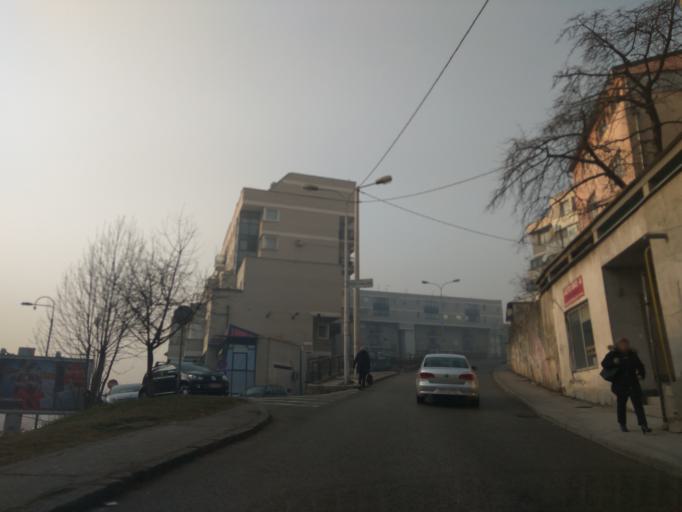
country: BA
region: Federation of Bosnia and Herzegovina
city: Kobilja Glava
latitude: 43.8590
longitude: 18.4031
